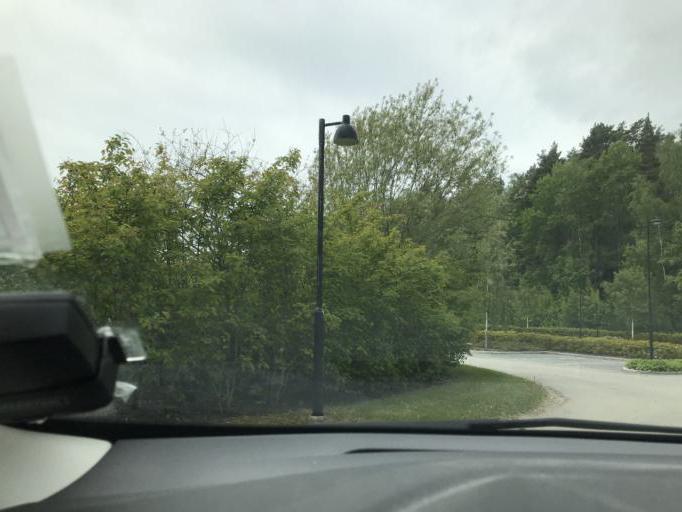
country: SE
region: Stockholm
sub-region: Botkyrka Kommun
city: Alby
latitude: 59.2182
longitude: 17.8478
